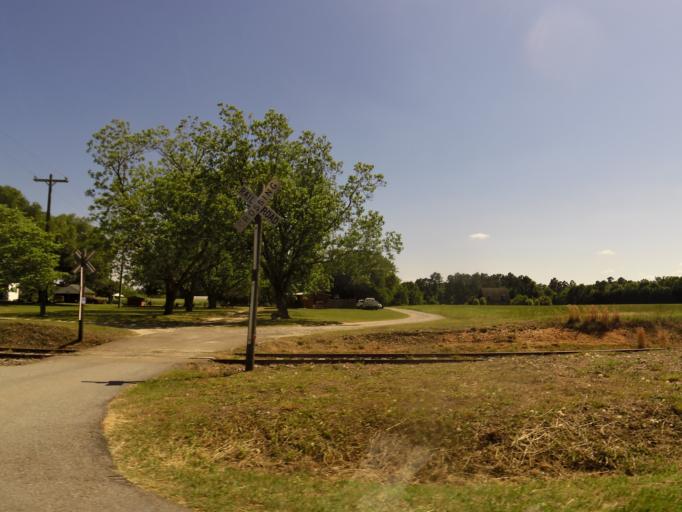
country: US
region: South Carolina
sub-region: Aiken County
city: Aiken
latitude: 33.5238
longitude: -81.6182
